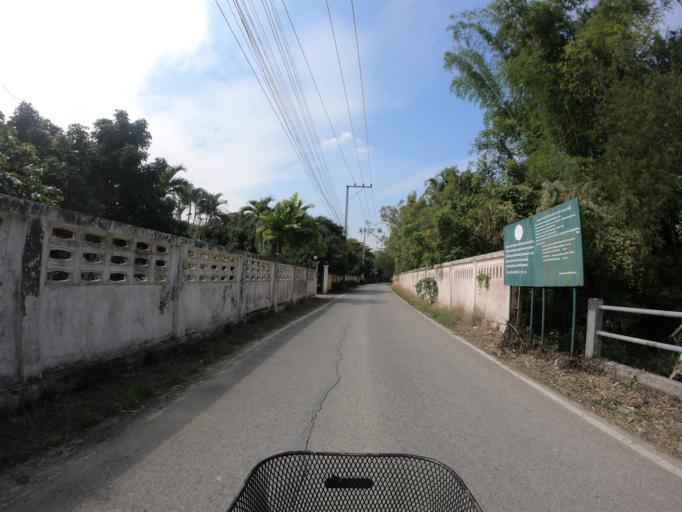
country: TH
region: Chiang Mai
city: Saraphi
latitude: 18.7083
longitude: 99.0222
